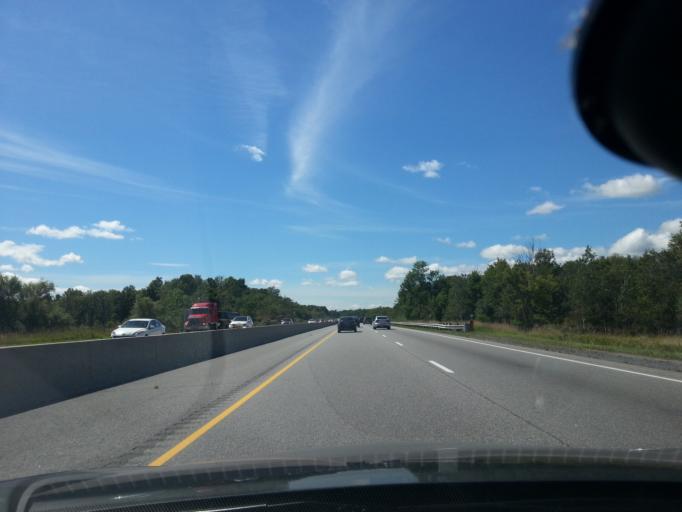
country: CA
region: Ontario
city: Gananoque
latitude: 44.3411
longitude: -76.1926
